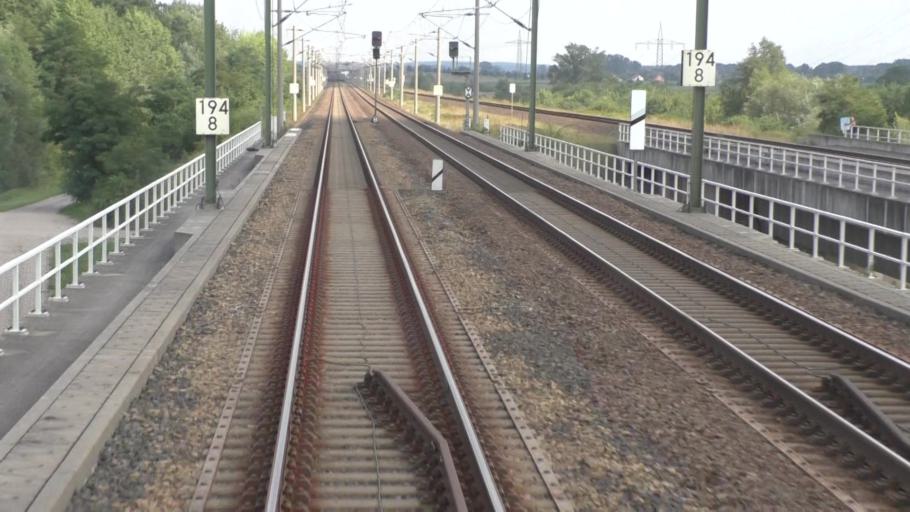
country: DE
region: Saxony-Anhalt
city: Schonhausen
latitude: 52.5967
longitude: 12.0057
